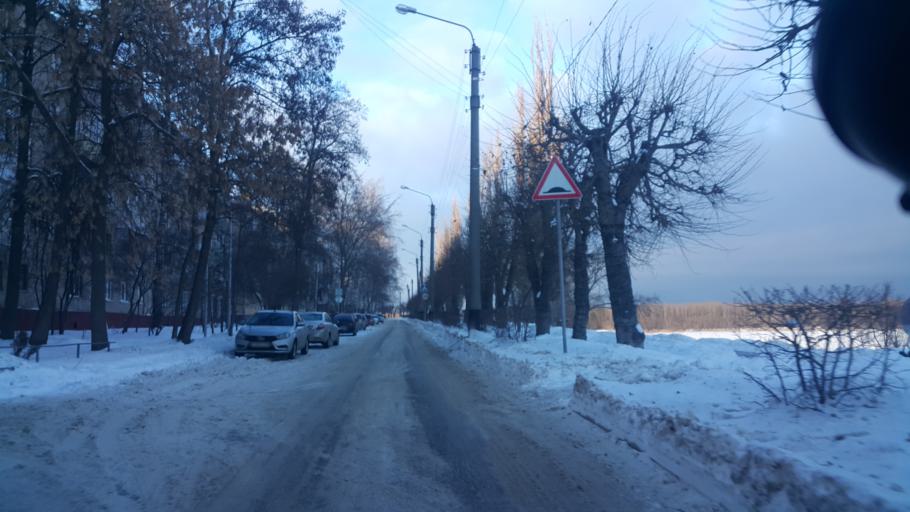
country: RU
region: Tambov
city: Tambov
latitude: 52.7016
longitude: 41.4799
